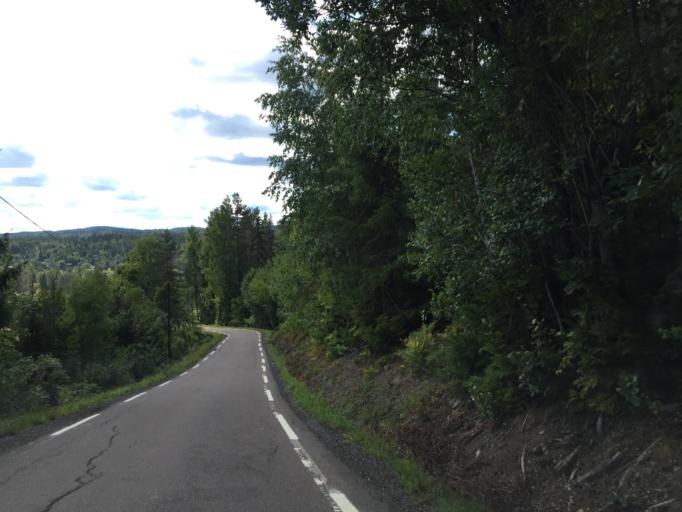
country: NO
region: Vestfold
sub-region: Hof
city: Hof
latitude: 59.4314
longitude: 10.1406
